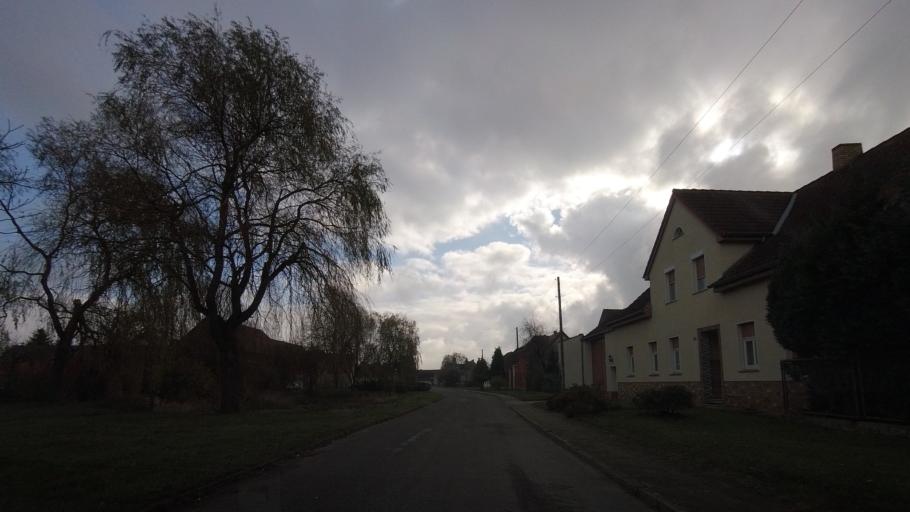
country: DE
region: Brandenburg
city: Niedergorsdorf
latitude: 52.0137
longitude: 12.9203
